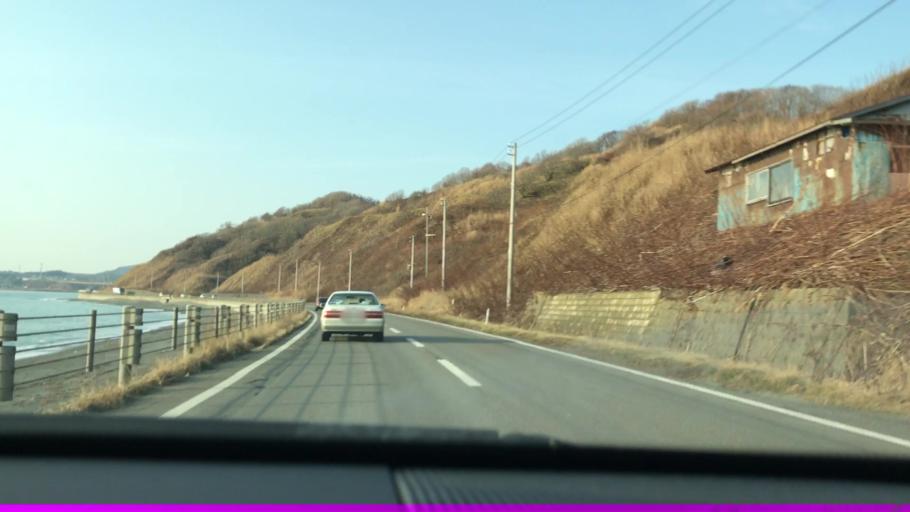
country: JP
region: Hokkaido
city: Shizunai-furukawacho
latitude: 42.2346
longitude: 142.6008
